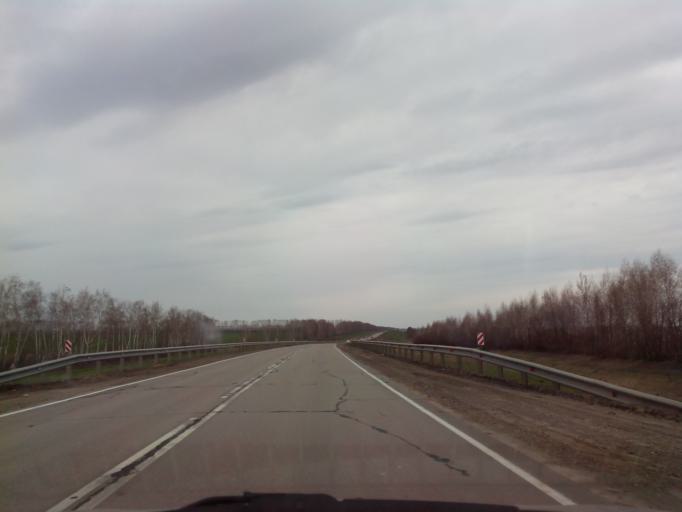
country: RU
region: Tambov
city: Znamenka
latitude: 52.4167
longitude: 41.3775
